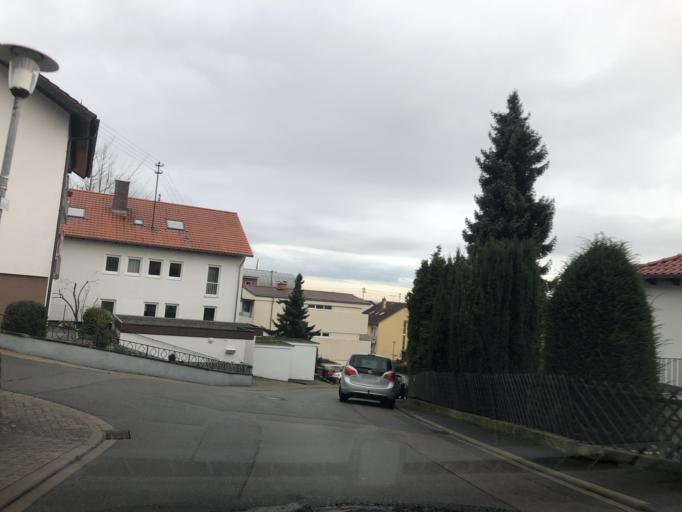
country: DE
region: Baden-Wuerttemberg
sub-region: Karlsruhe Region
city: Dossenheim
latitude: 49.4553
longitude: 8.6759
